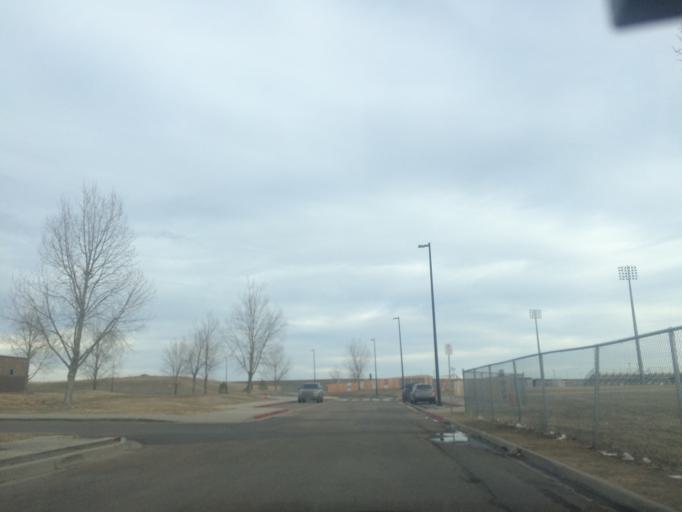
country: US
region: Colorado
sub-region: Boulder County
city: Erie
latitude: 40.0465
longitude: -105.0168
